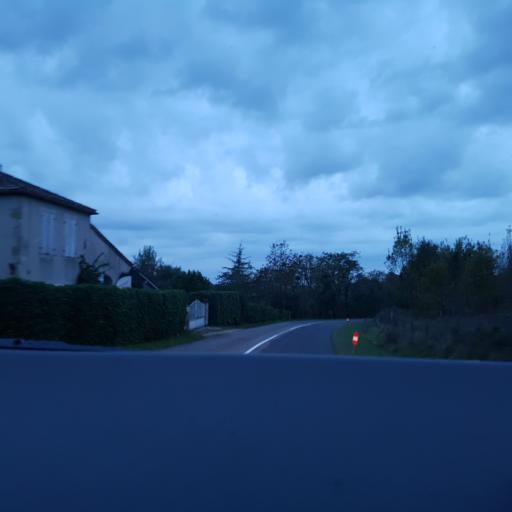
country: FR
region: Midi-Pyrenees
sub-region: Departement du Gers
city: Montreal
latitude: 43.9463
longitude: 0.1524
